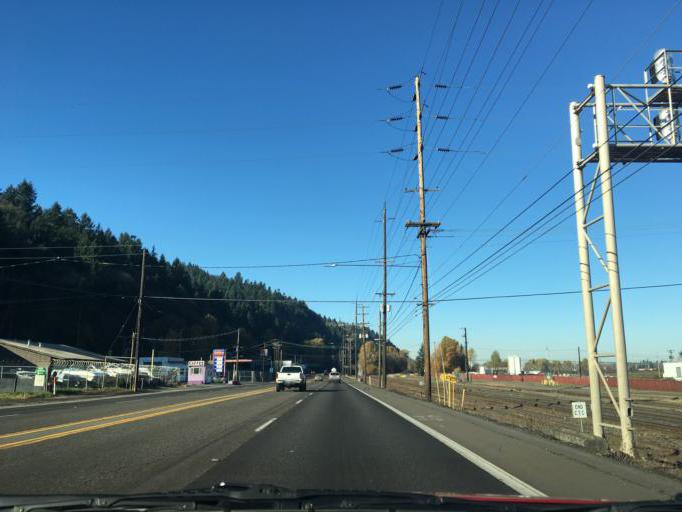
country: US
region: Oregon
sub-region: Washington County
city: West Haven
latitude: 45.5651
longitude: -122.7478
